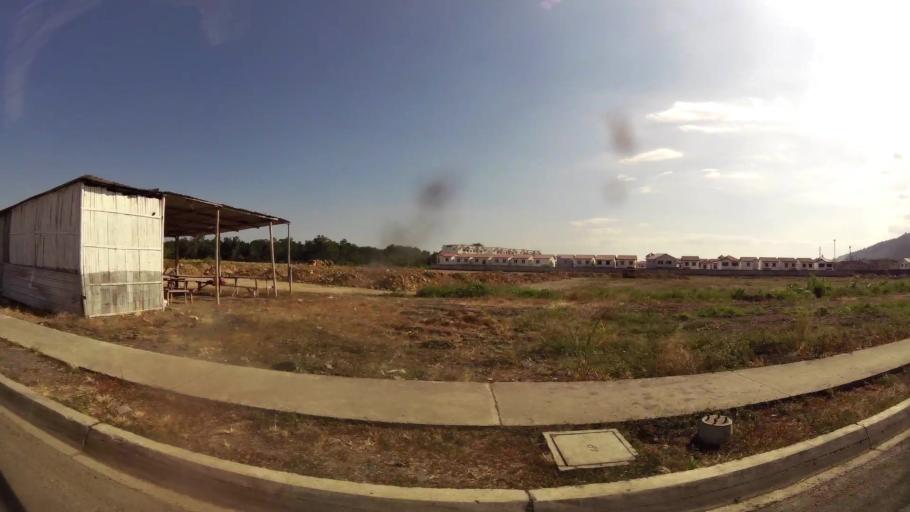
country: EC
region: Guayas
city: Santa Lucia
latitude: -2.1895
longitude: -80.0008
